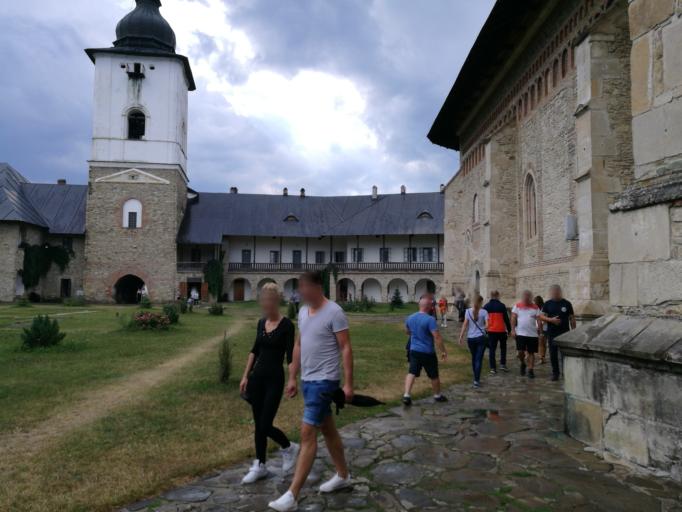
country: RO
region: Neamt
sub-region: Comuna Vanatori Neamt
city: Nemtisor
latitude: 47.2635
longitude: 26.2095
